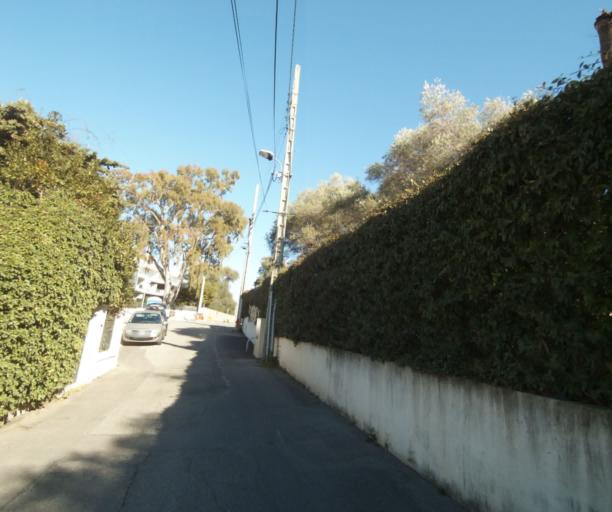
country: FR
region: Provence-Alpes-Cote d'Azur
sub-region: Departement des Alpes-Maritimes
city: Antibes
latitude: 43.5642
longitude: 7.1198
